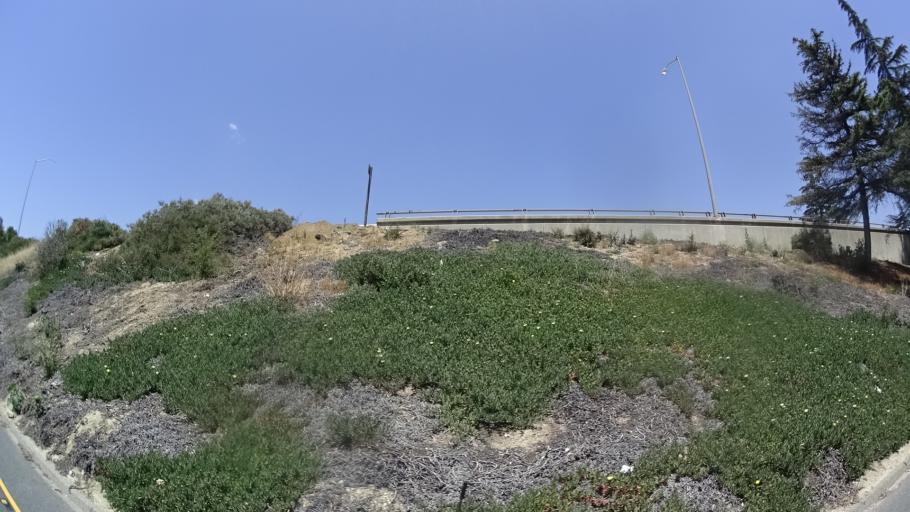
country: US
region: California
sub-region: Los Angeles County
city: La Crescenta-Montrose
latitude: 34.2096
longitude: -118.2244
